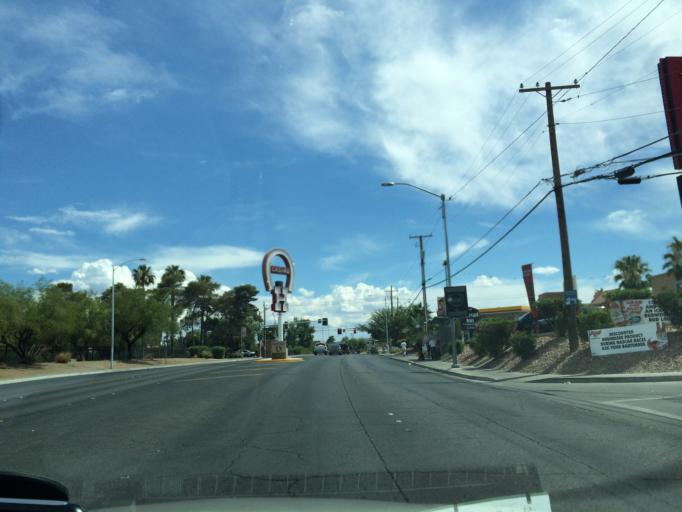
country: US
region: Nevada
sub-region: Clark County
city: Las Vegas
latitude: 36.1825
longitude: -115.1341
